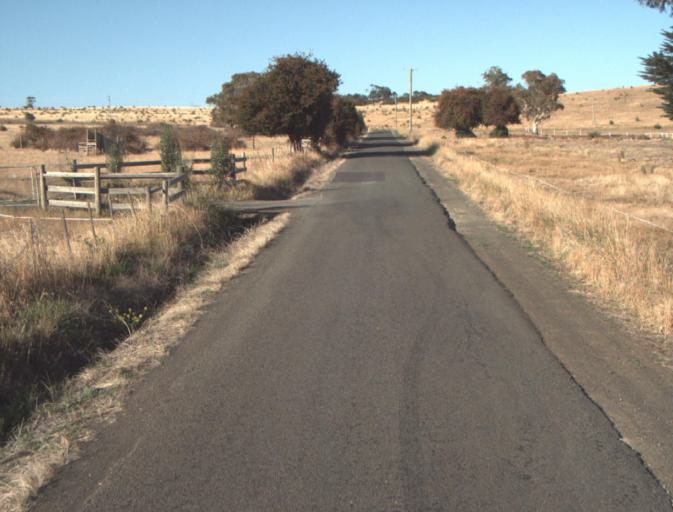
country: AU
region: Tasmania
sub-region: Launceston
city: Newstead
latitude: -41.4360
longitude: 147.2120
